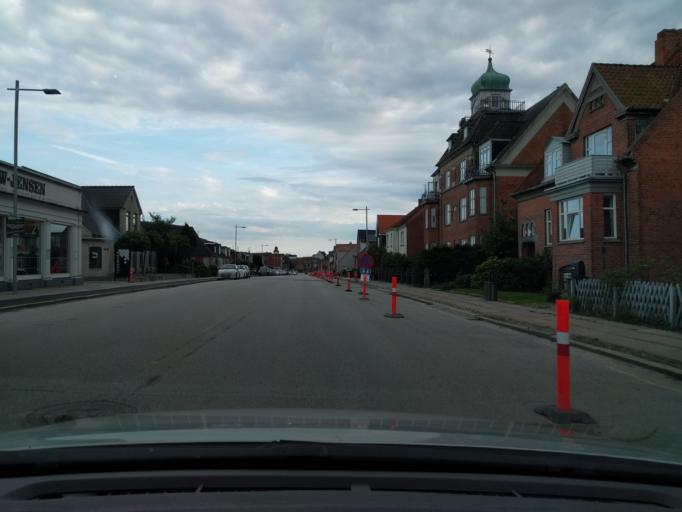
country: DK
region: Zealand
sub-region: Guldborgsund Kommune
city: Nykobing Falster
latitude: 54.7768
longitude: 11.8670
